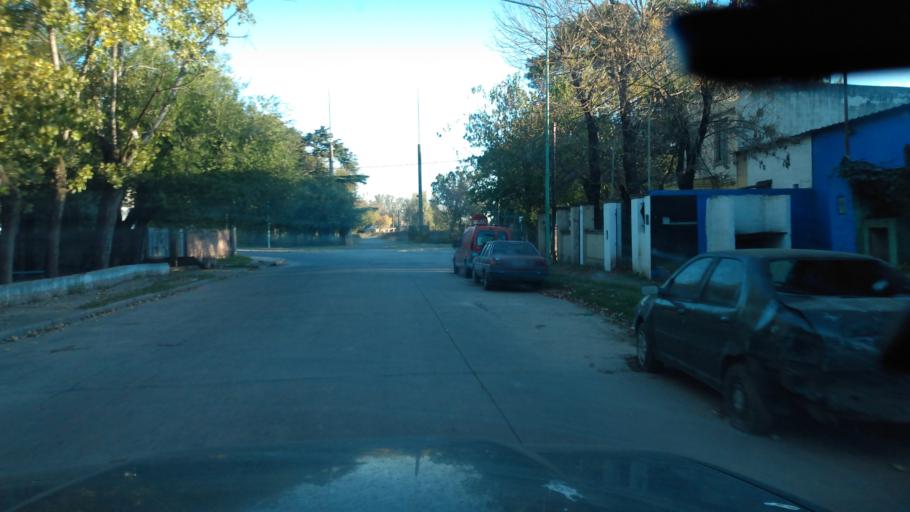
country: AR
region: Buenos Aires
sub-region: Partido de Lujan
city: Lujan
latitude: -34.5664
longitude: -59.1249
